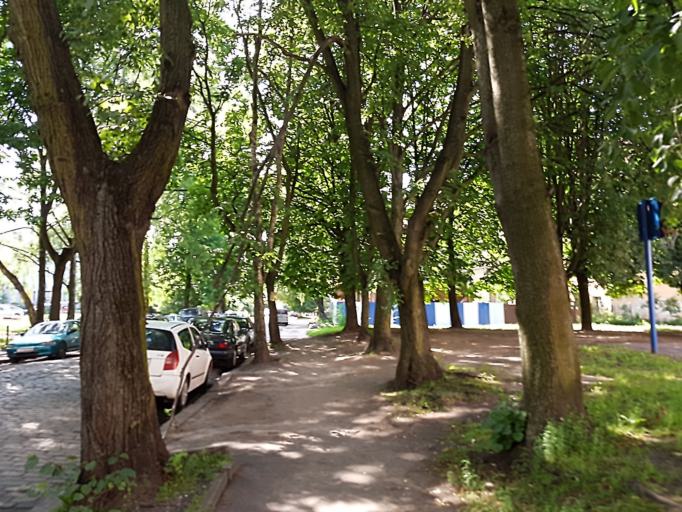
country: RU
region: Kaliningrad
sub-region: Gorod Kaliningrad
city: Kaliningrad
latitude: 54.7004
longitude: 20.5131
